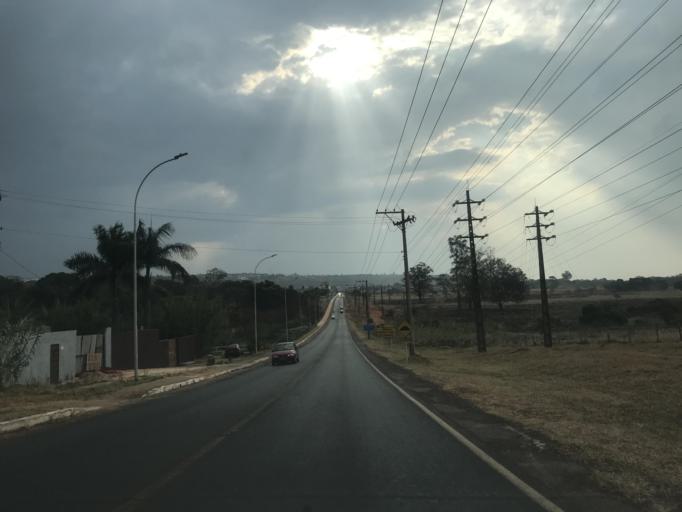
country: BR
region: Federal District
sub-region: Brasilia
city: Brasilia
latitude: -15.6638
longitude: -47.8248
